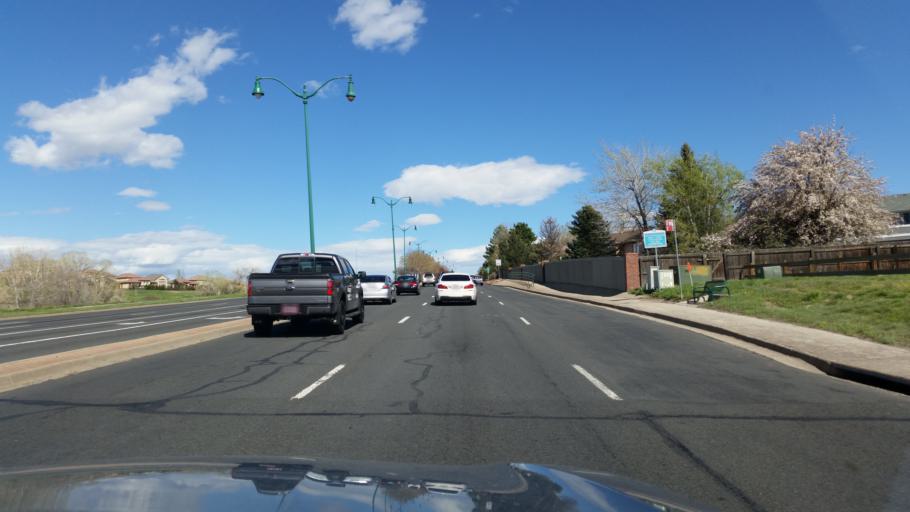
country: US
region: Colorado
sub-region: Broomfield County
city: Broomfield
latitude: 39.8852
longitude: -105.0527
